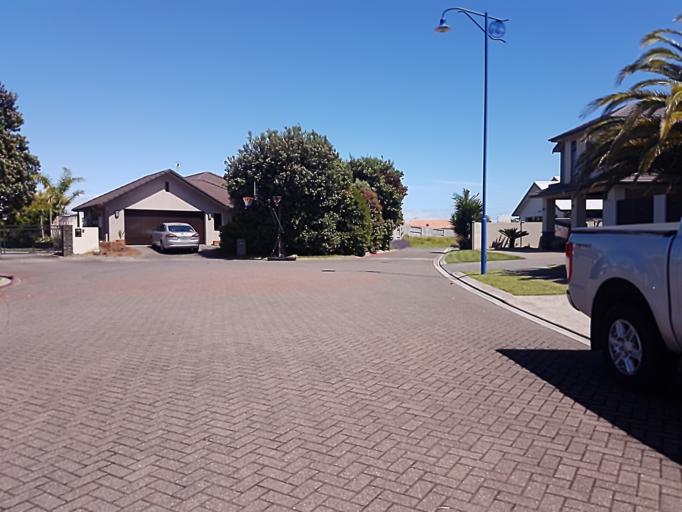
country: NZ
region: Bay of Plenty
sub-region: Tauranga City
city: Tauranga
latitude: -37.6911
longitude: 176.2679
